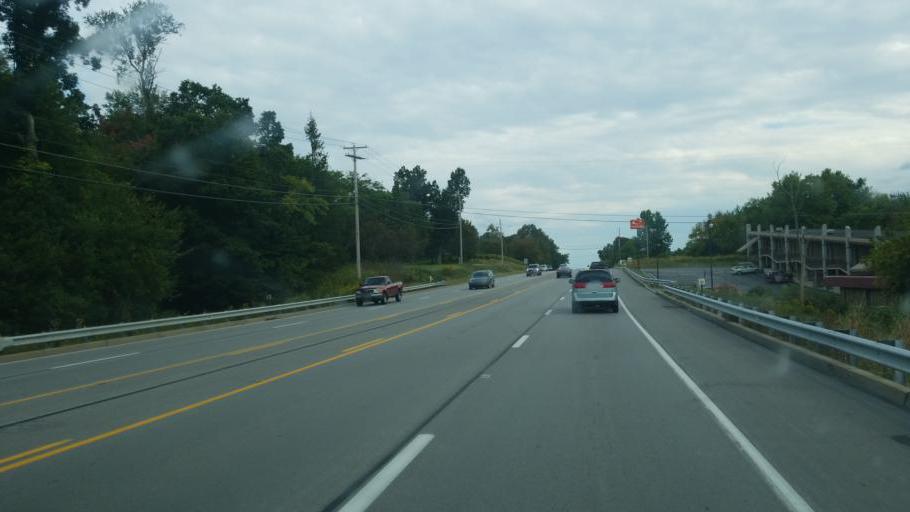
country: US
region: Pennsylvania
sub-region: Mercer County
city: Hermitage
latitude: 41.1968
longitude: -80.4564
